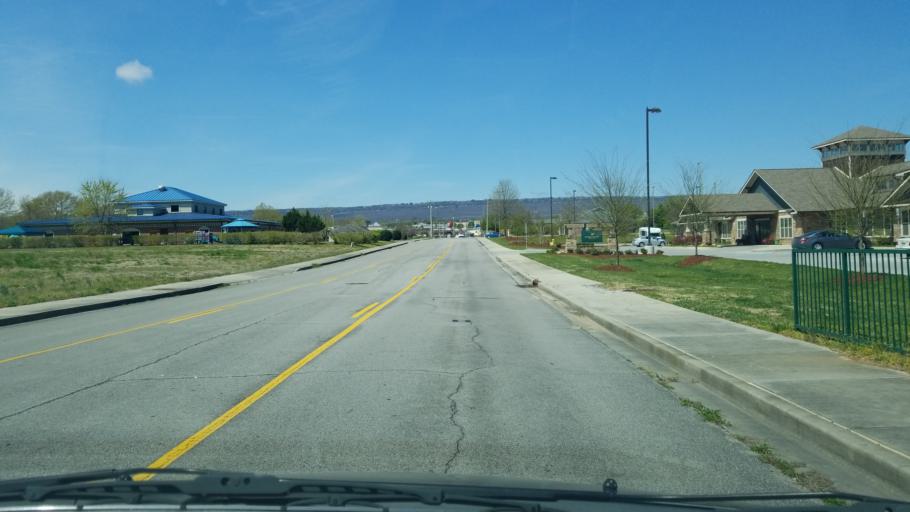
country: US
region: Tennessee
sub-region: Hamilton County
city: Red Bank
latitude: 35.1337
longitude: -85.2350
